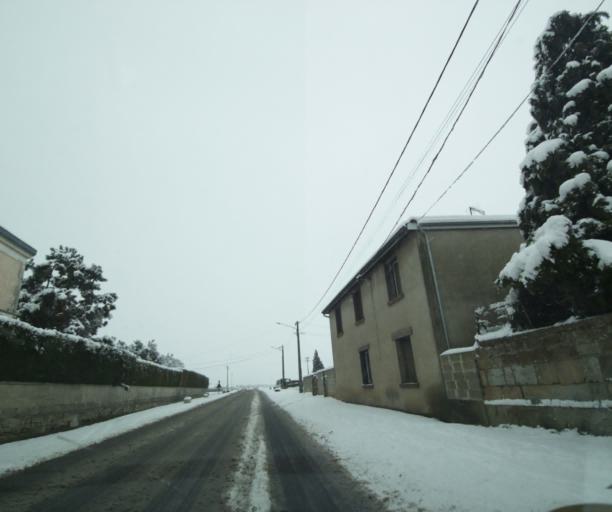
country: FR
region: Champagne-Ardenne
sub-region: Departement de la Haute-Marne
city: Saint-Dizier
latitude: 48.5819
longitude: 4.9041
